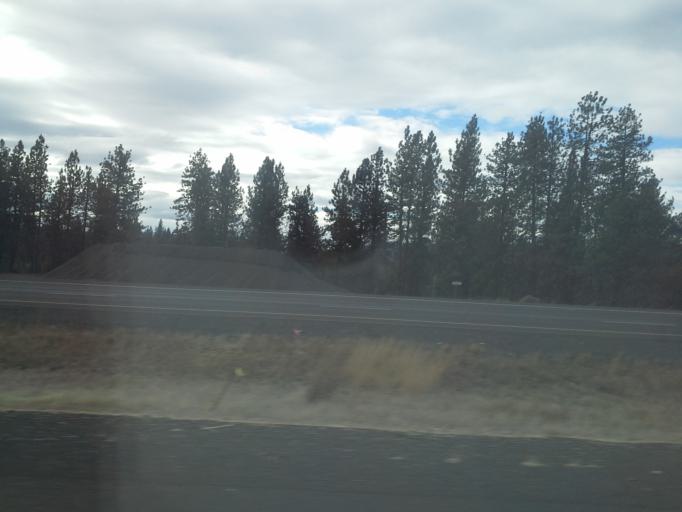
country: US
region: Oregon
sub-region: Union County
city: La Grande
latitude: 45.3694
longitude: -118.2921
